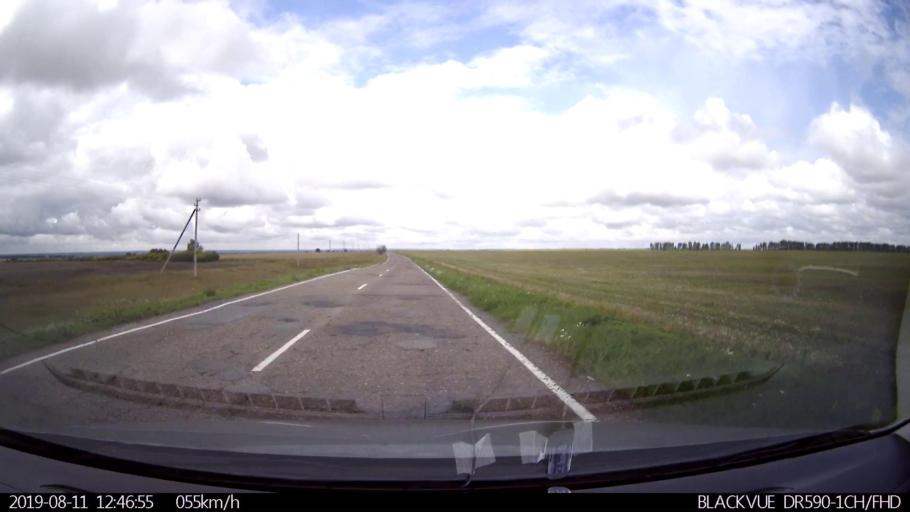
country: RU
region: Ulyanovsk
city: Ignatovka
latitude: 53.8668
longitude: 47.7140
